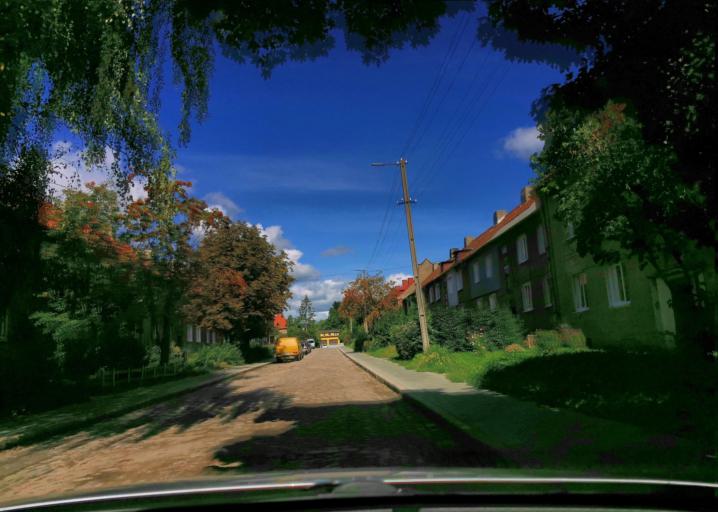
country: RU
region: Kaliningrad
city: Chernyakhovsk
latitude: 54.6361
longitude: 21.8401
